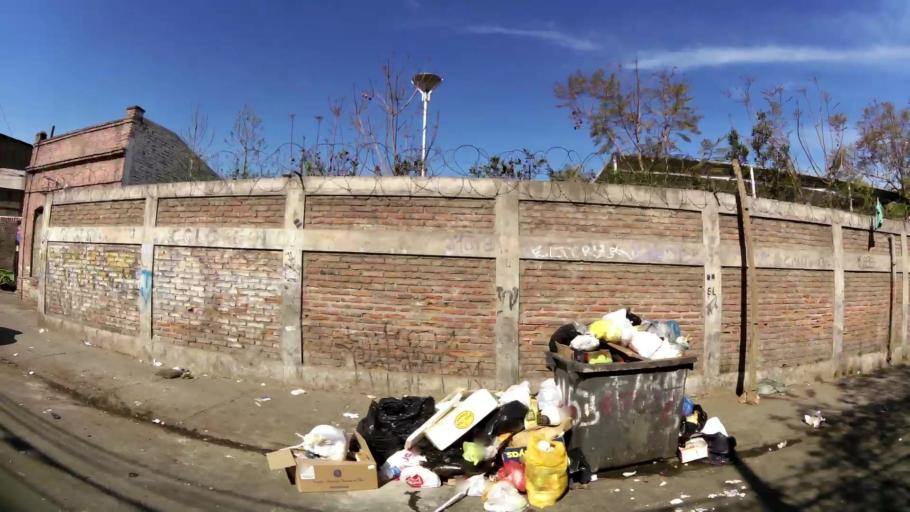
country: CL
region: Santiago Metropolitan
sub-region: Provincia de Santiago
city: Santiago
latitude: -33.4265
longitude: -70.6499
